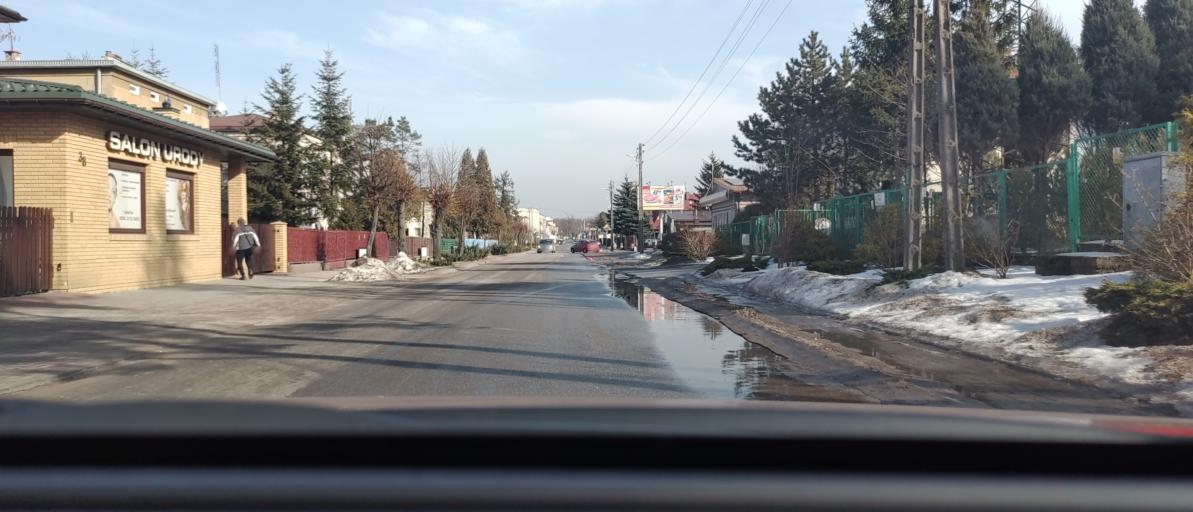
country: PL
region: Masovian Voivodeship
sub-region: Powiat bialobrzeski
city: Bialobrzegi
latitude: 51.6451
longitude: 20.9481
